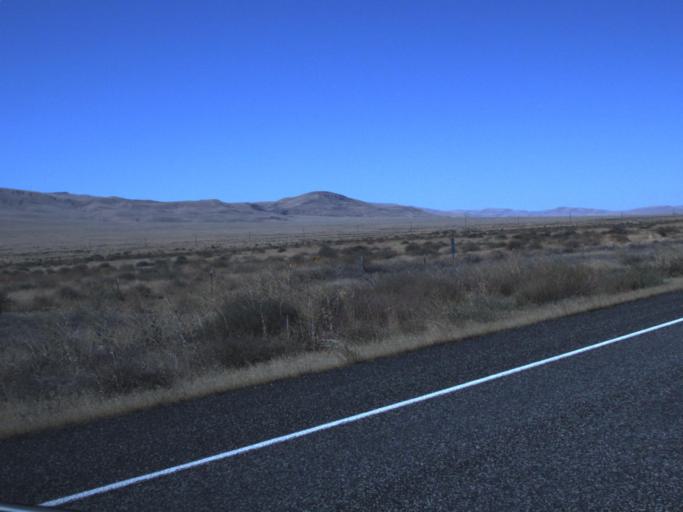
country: US
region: Washington
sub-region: Benton County
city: Benton City
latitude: 46.4611
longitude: -119.5288
